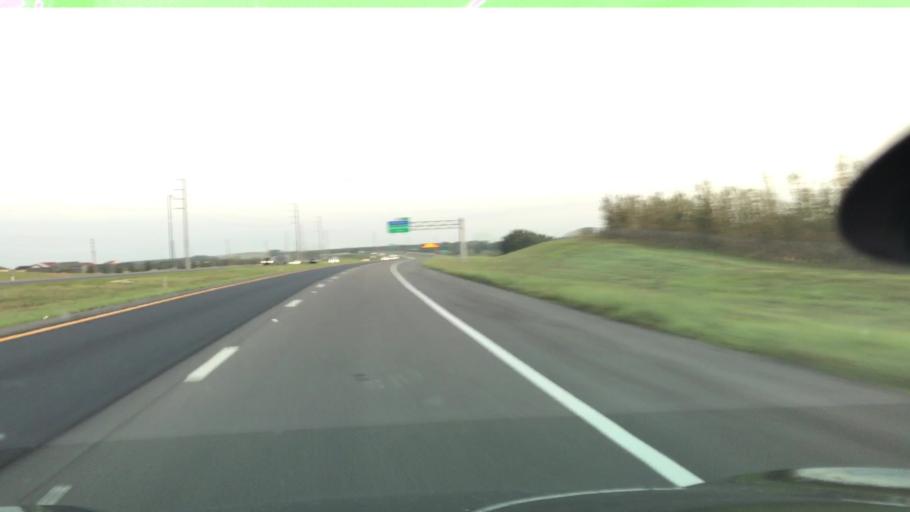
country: US
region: Florida
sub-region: Polk County
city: Citrus Ridge
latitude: 28.4261
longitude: -81.6348
